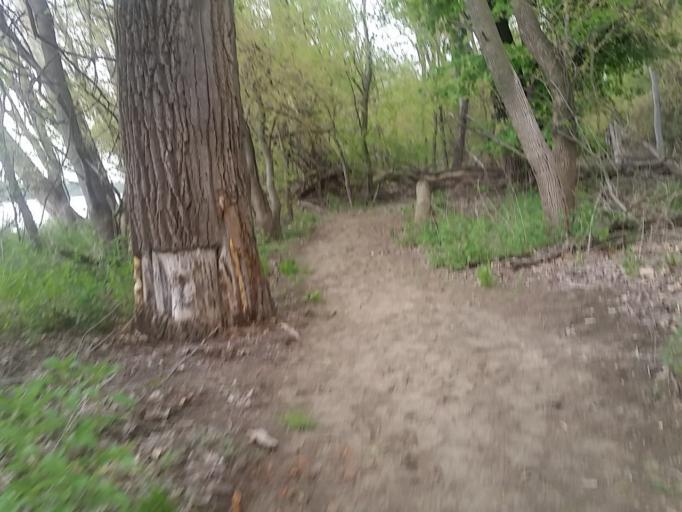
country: US
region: Nebraska
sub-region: Sarpy County
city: Bellevue
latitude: 41.1841
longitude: -95.8954
